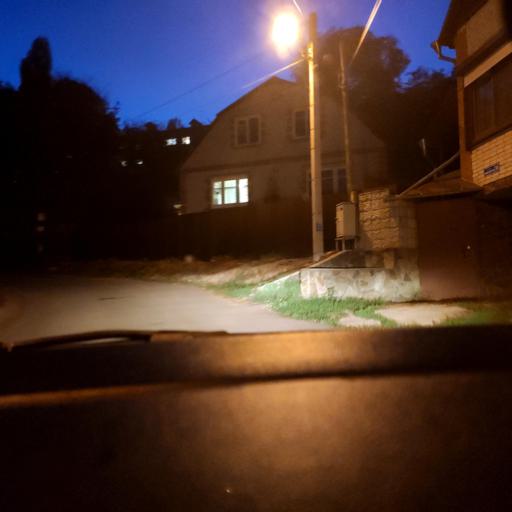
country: RU
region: Voronezj
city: Voronezh
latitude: 51.6287
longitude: 39.1806
